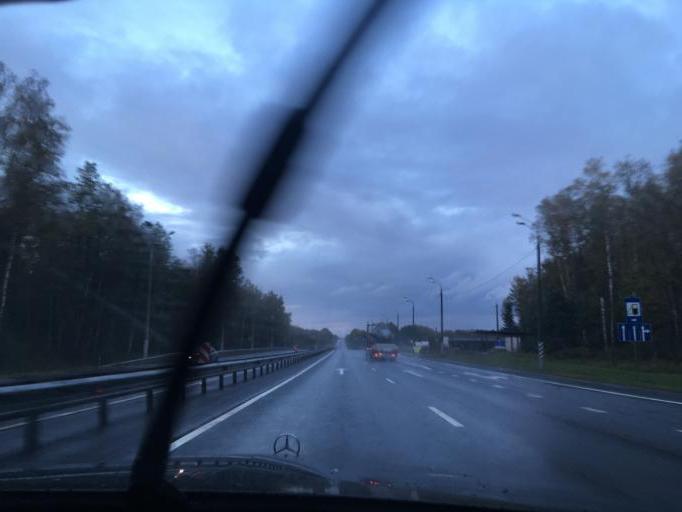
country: RU
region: Smolensk
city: Yartsevo
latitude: 55.0936
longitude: 32.8481
